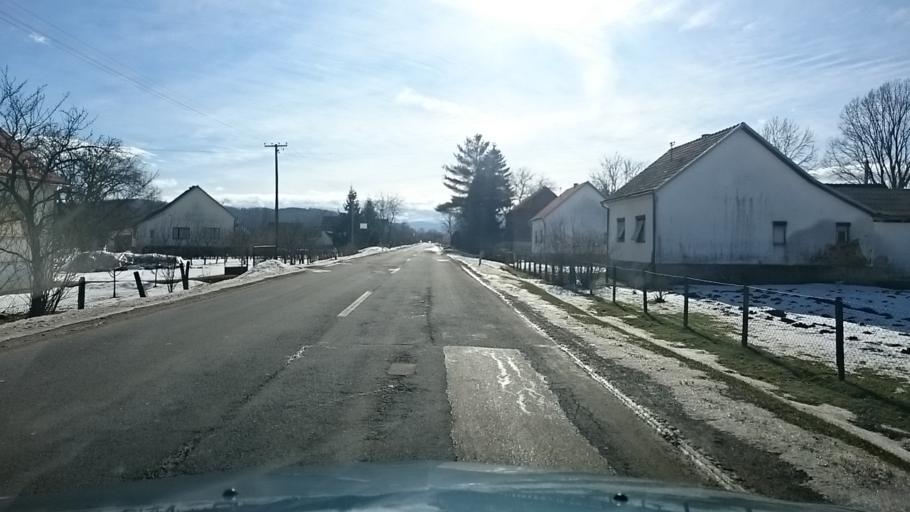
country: BA
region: Republika Srpska
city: Bosanska Dubica
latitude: 45.2132
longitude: 16.9045
